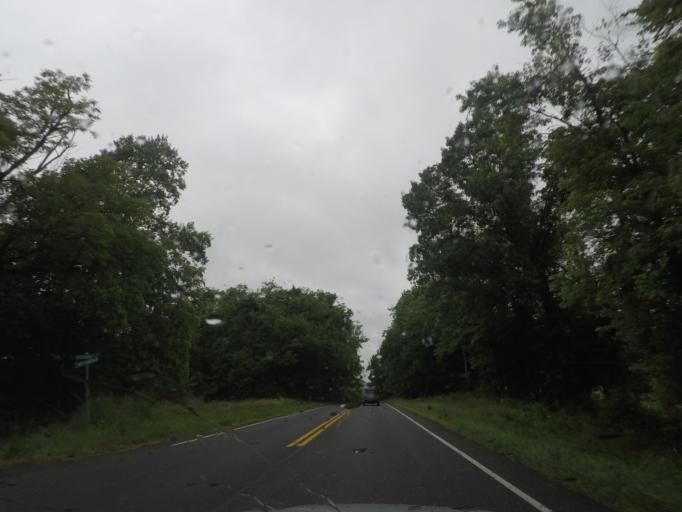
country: US
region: Virginia
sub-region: Orange County
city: Orange
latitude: 38.2762
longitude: -78.1333
